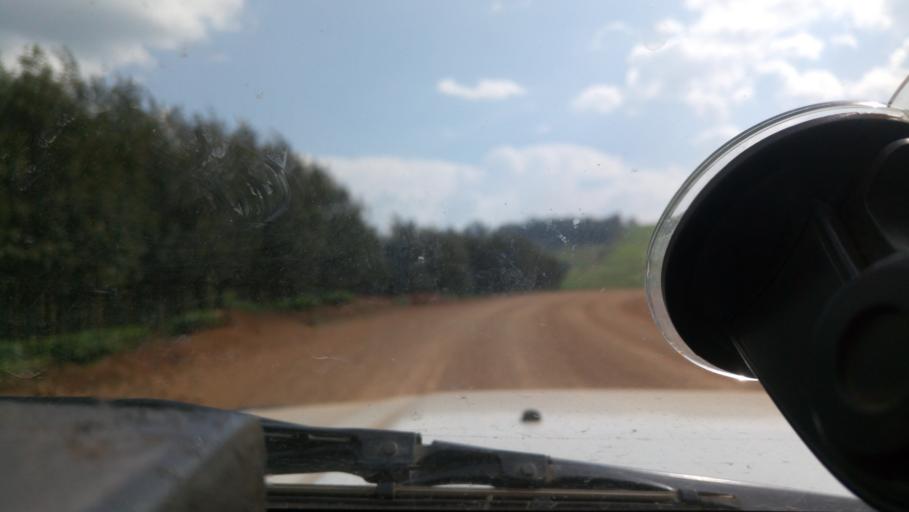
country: KE
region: Nyamira District
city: Nyamira
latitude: -0.5723
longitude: 35.0490
